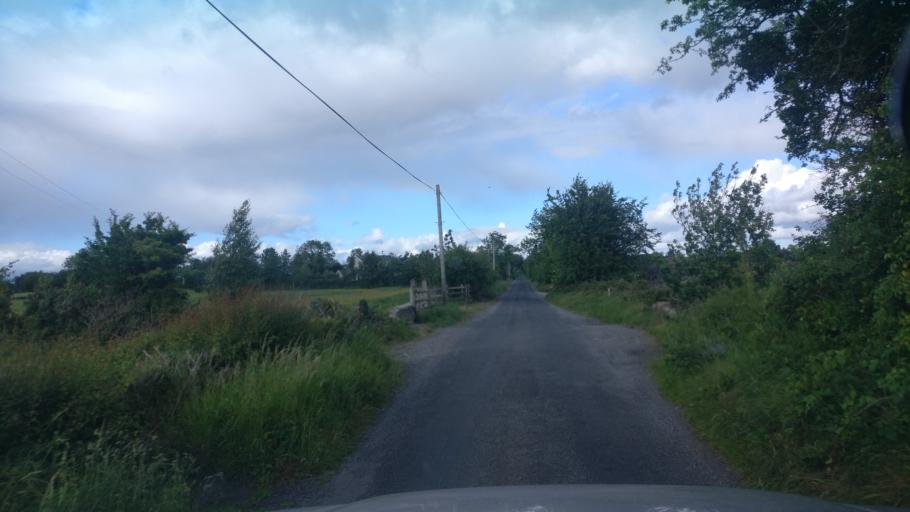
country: IE
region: Connaught
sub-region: County Galway
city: Loughrea
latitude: 53.1941
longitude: -8.3796
